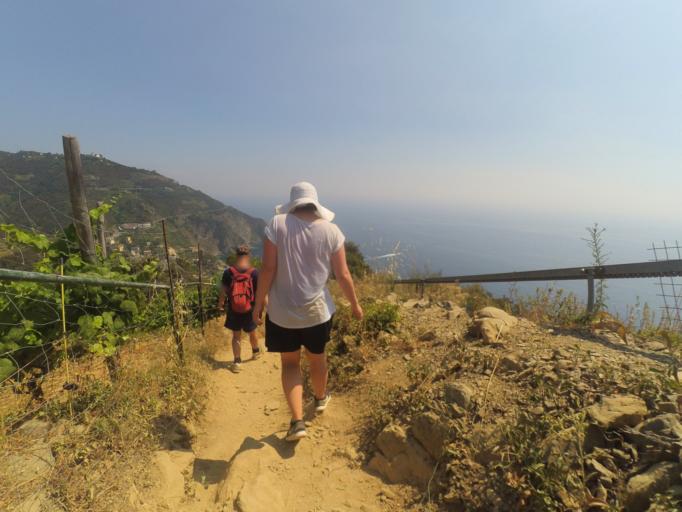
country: IT
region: Liguria
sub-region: Provincia di La Spezia
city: Riomaggiore
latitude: 44.1045
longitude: 9.7328
